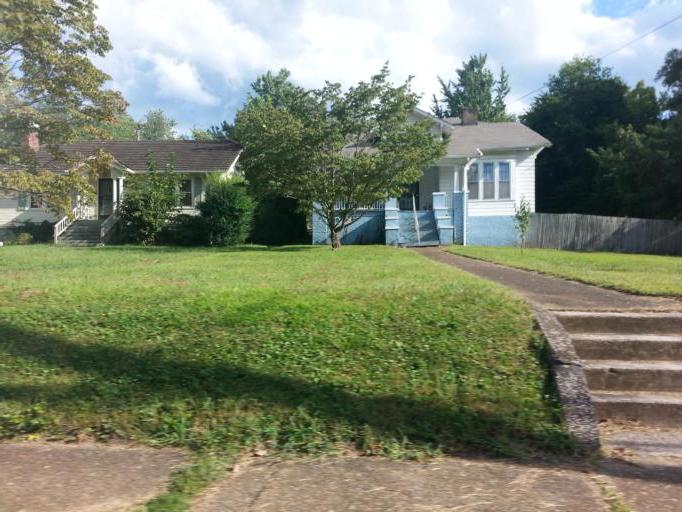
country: US
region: Tennessee
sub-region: Knox County
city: Knoxville
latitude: 36.0010
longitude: -83.9202
